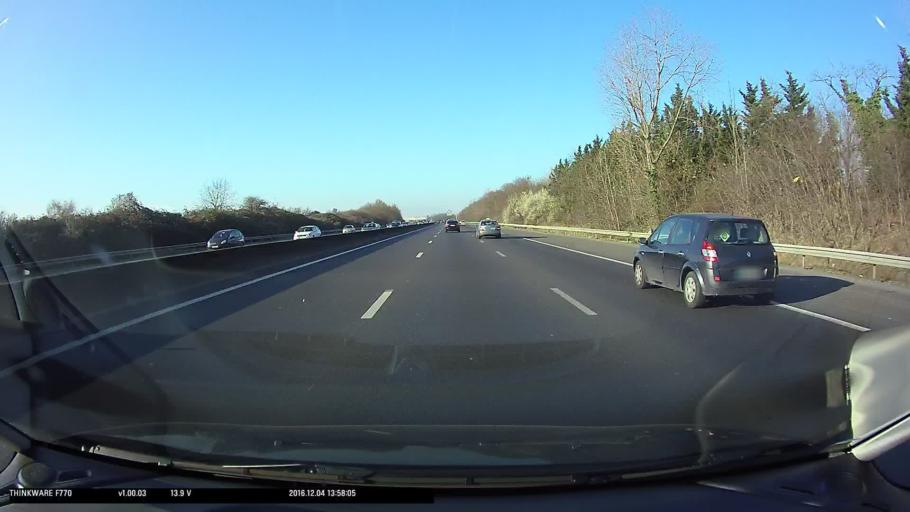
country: FR
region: Ile-de-France
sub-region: Departement du Val-d'Oise
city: Herblay
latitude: 49.0042
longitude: 2.1673
